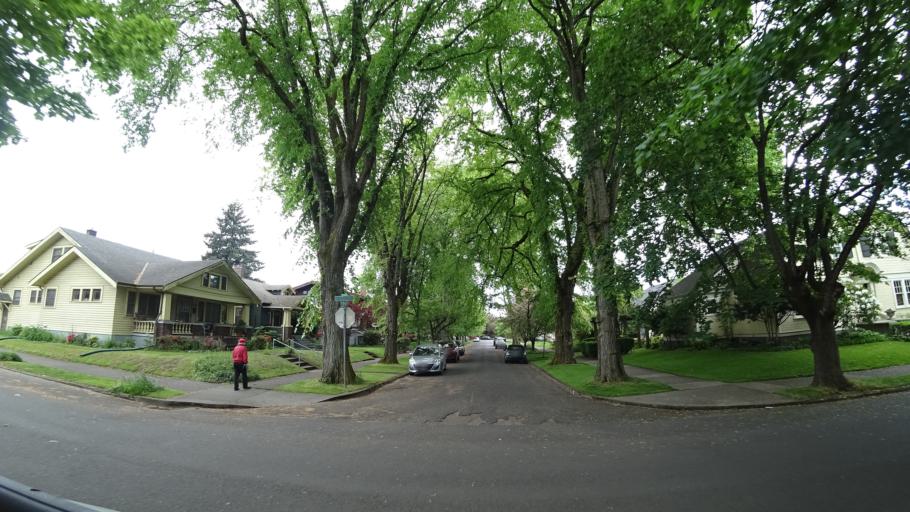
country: US
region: Oregon
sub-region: Multnomah County
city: Portland
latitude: 45.5085
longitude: -122.6463
